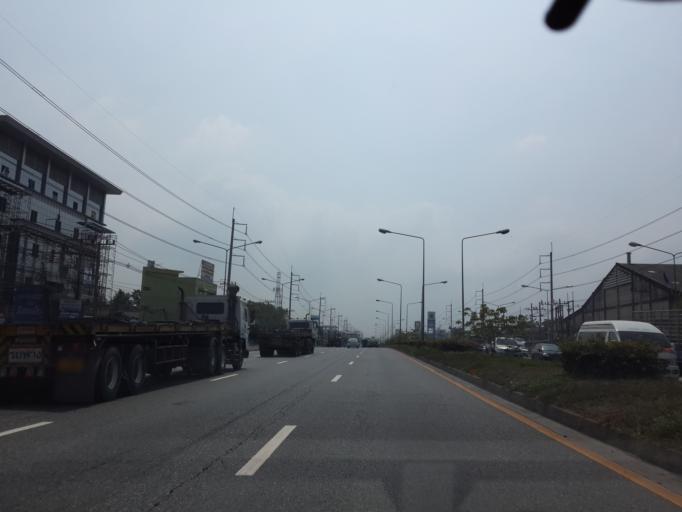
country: TH
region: Chon Buri
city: Chon Buri
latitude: 13.3988
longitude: 101.0066
